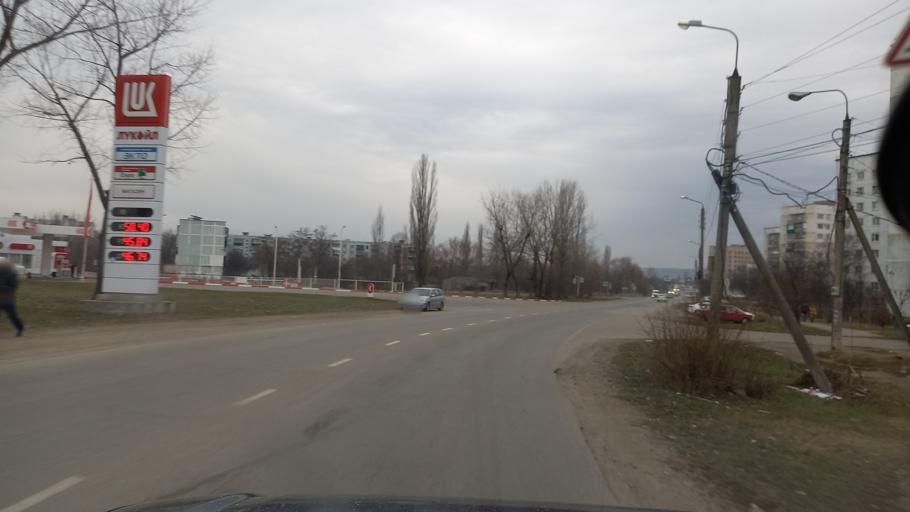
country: RU
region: Adygeya
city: Maykop
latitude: 44.5798
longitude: 40.1359
